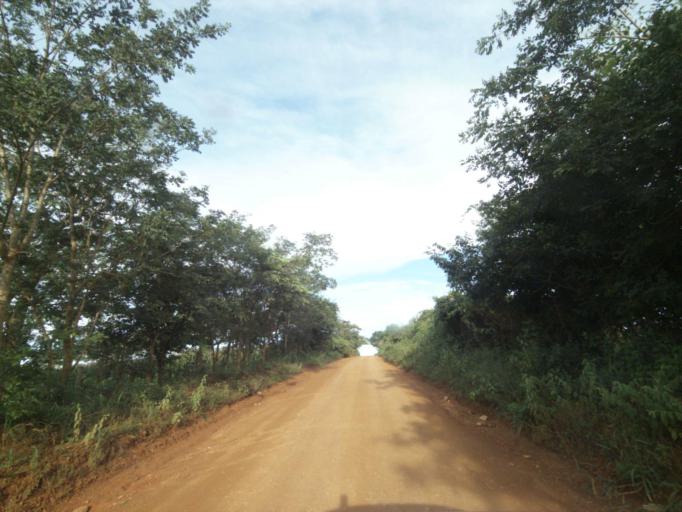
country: BR
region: Goias
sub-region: Jaragua
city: Jaragua
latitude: -15.8891
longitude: -49.4715
